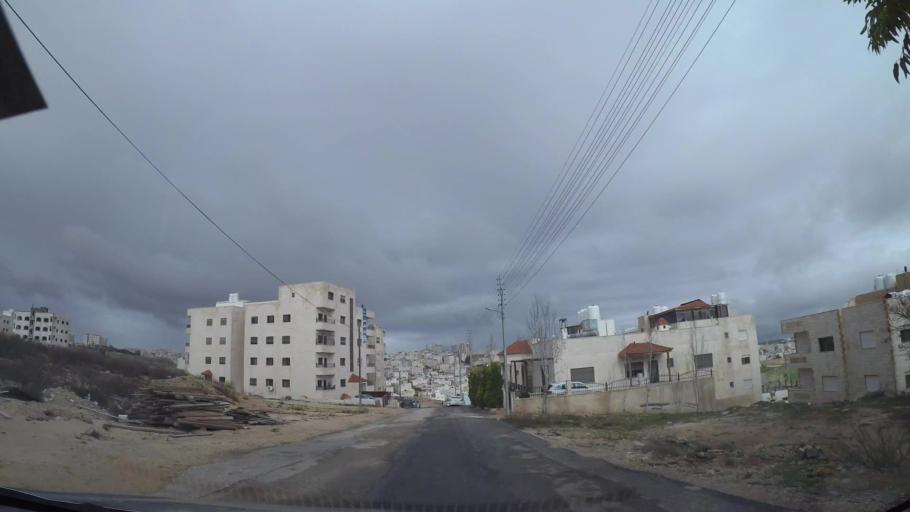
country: JO
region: Amman
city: Al Jubayhah
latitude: 32.0621
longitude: 35.8886
